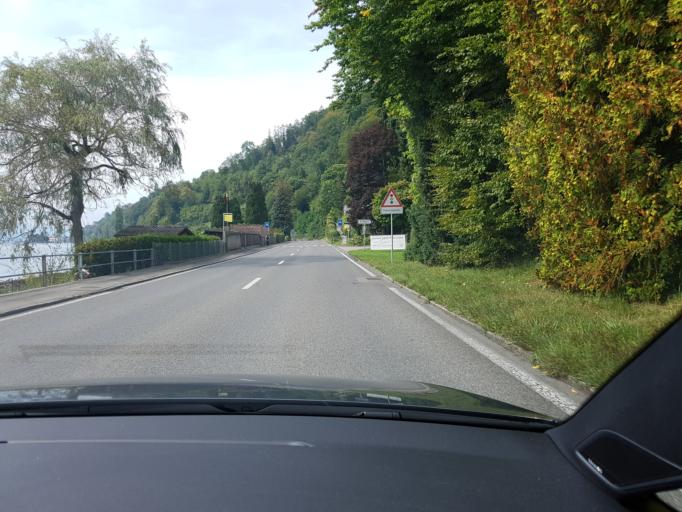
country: CH
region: Bern
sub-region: Thun District
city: Sigriswil
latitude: 46.7062
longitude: 7.7267
